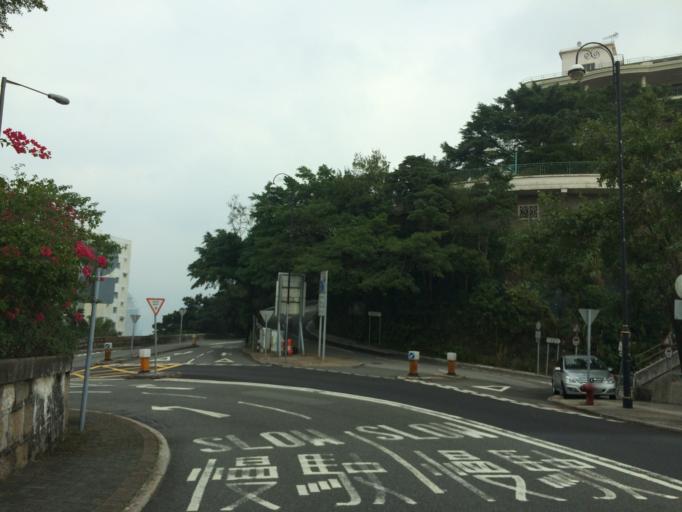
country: HK
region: Wanchai
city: Wan Chai
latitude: 22.2690
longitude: 114.1653
